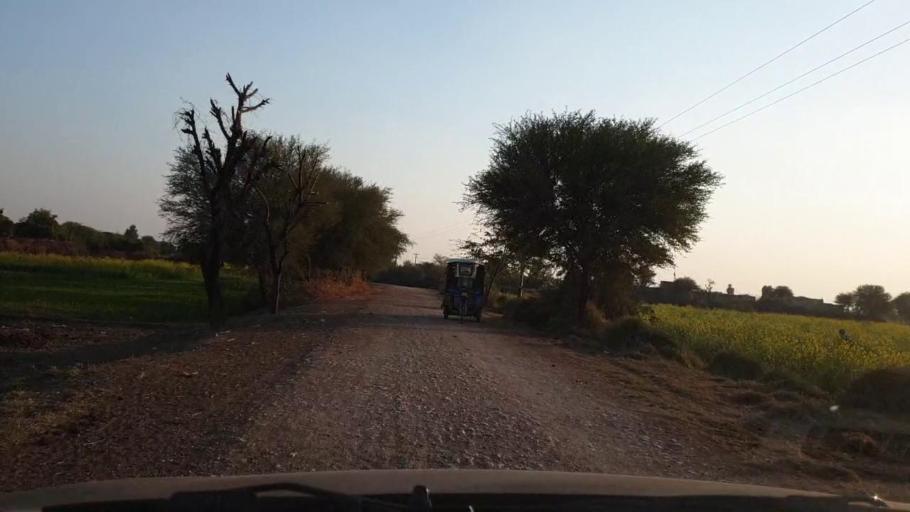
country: PK
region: Sindh
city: Jhol
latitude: 25.9201
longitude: 68.9336
